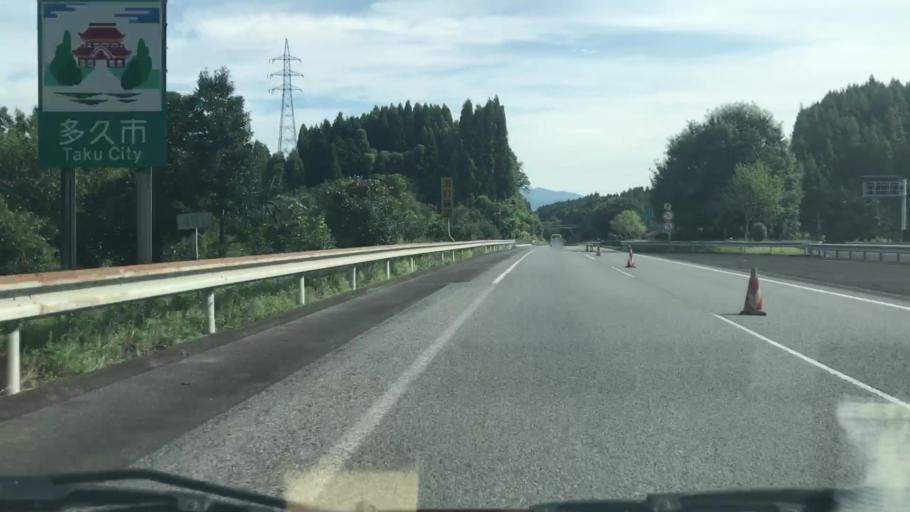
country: JP
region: Saga Prefecture
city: Takeocho-takeo
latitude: 33.2451
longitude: 130.0688
